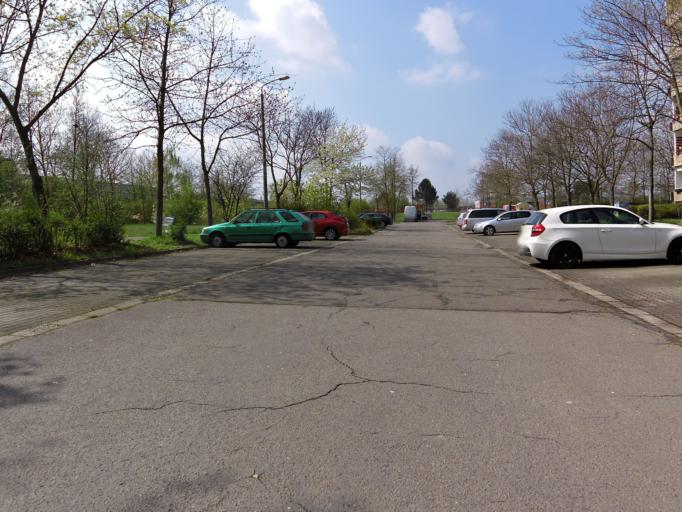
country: DE
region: Saxony
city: Markranstadt
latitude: 51.3226
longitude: 12.2713
